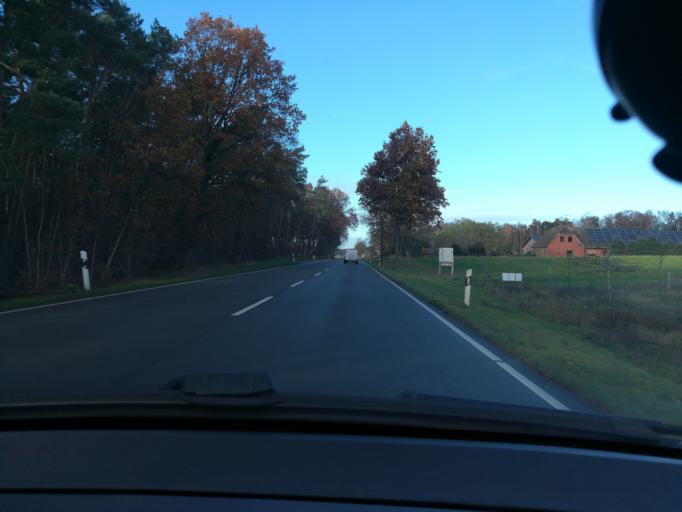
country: DE
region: Lower Saxony
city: Kirchdorf
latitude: 52.5476
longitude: 8.8631
